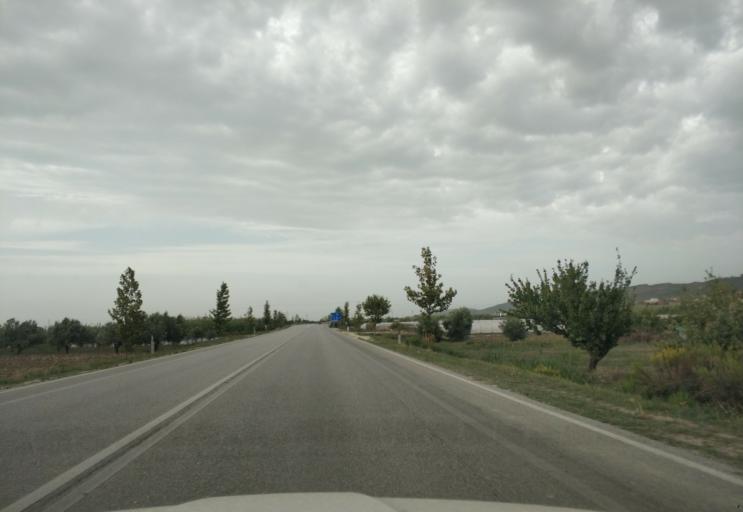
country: AL
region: Fier
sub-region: Rrethi i Fierit
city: Frakulla e Madhe
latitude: 40.6283
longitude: 19.5108
